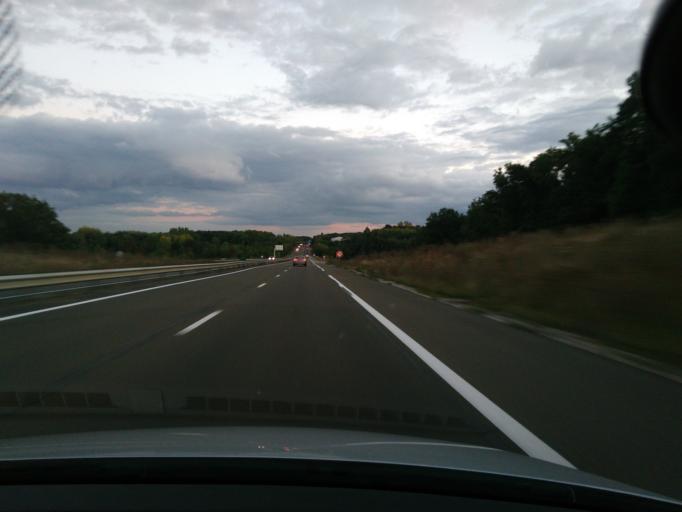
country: FR
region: Ile-de-France
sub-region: Departement de Seine-et-Marne
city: Quincy-Voisins
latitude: 48.9053
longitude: 2.8867
